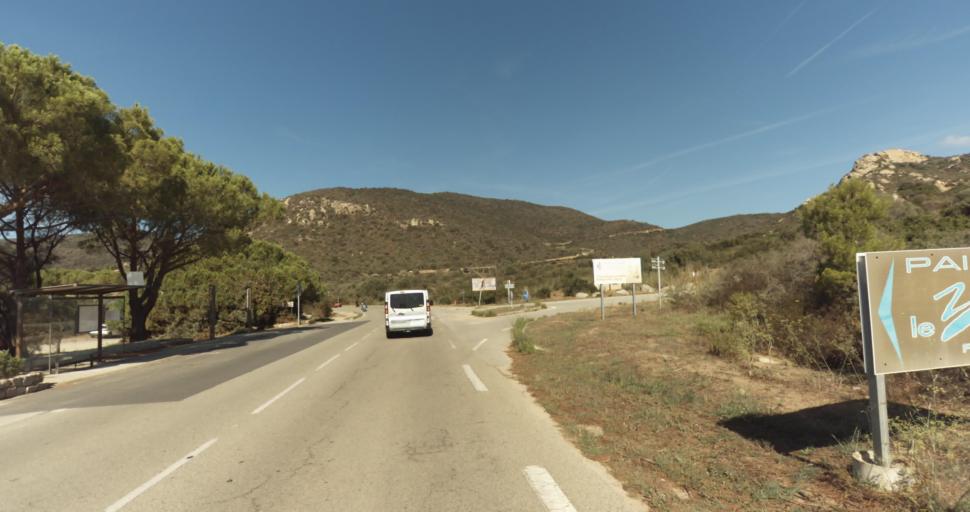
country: FR
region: Corsica
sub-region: Departement de la Corse-du-Sud
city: Ajaccio
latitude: 41.9104
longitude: 8.6479
